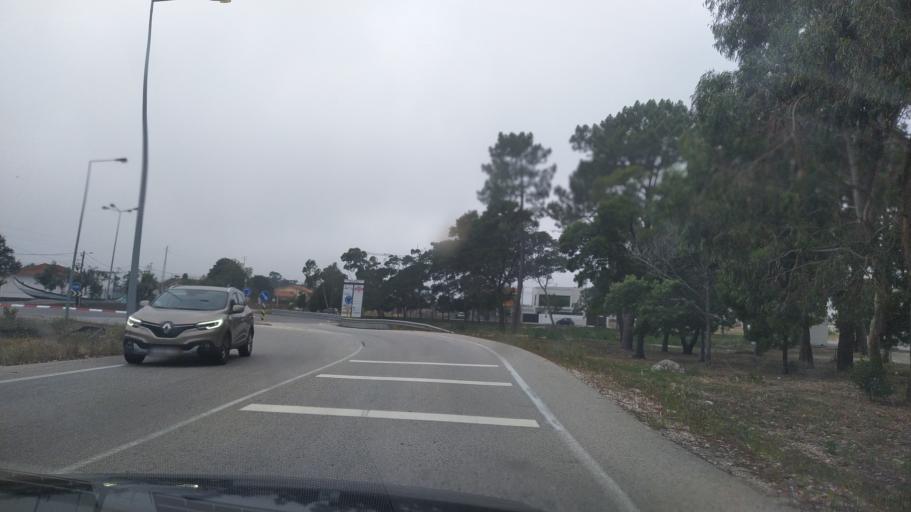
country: PT
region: Aveiro
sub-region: Ilhavo
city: Gafanha da Encarnacao
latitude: 40.6131
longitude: -8.7193
